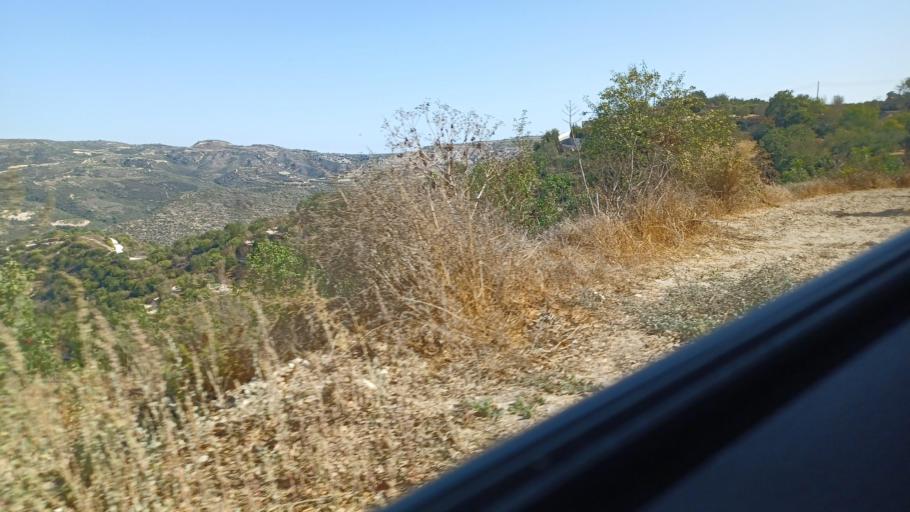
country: CY
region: Pafos
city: Tala
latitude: 34.8606
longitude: 32.4498
